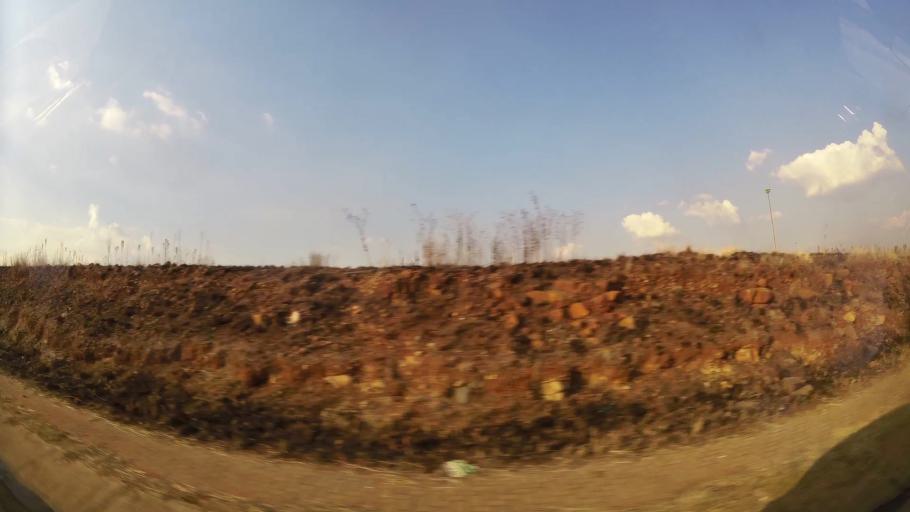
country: ZA
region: Gauteng
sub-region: Ekurhuleni Metropolitan Municipality
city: Germiston
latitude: -26.3596
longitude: 28.2207
